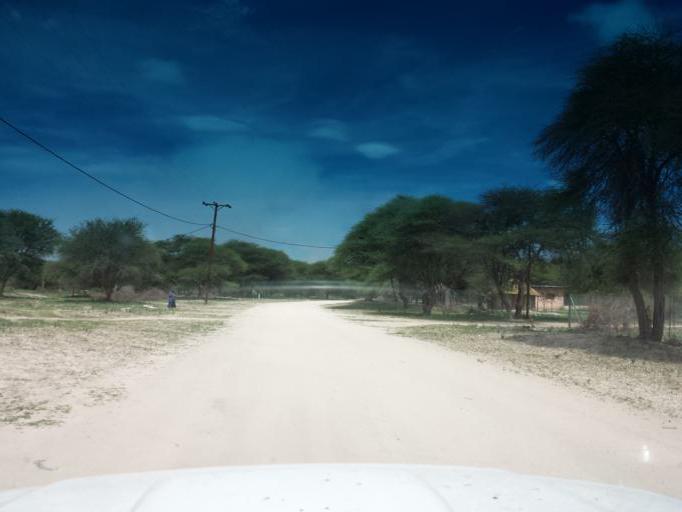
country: BW
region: North West
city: Shakawe
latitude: -18.7423
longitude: 22.1796
